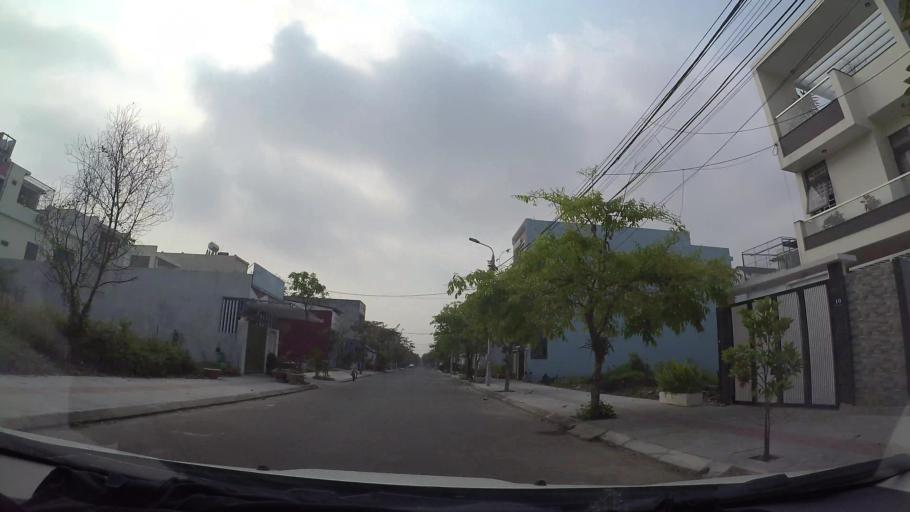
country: VN
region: Da Nang
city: Cam Le
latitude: 16.0099
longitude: 108.2166
